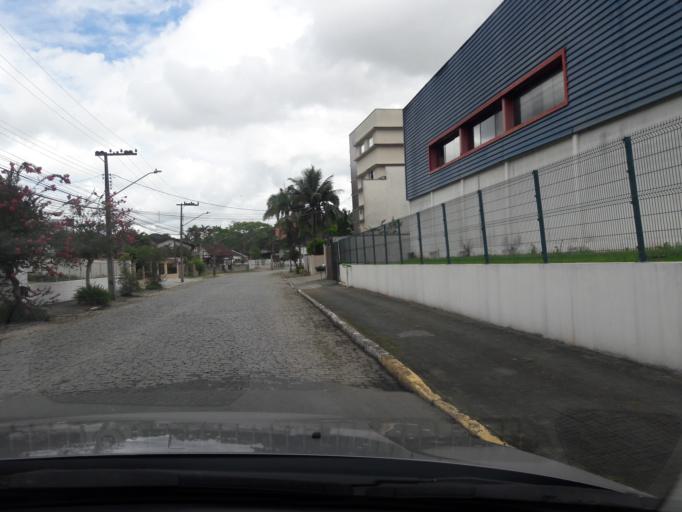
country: BR
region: Santa Catarina
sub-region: Joinville
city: Joinville
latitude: -26.3231
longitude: -48.8586
